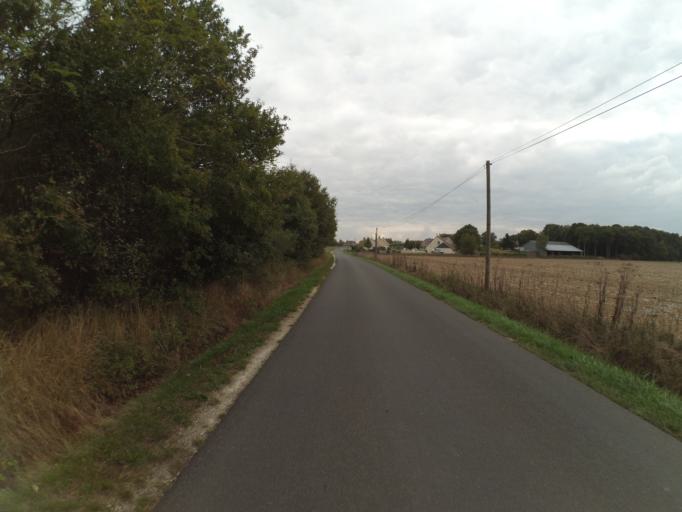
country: FR
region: Centre
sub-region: Departement d'Indre-et-Loire
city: Nazelles-Negron
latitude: 47.4893
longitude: 0.9430
